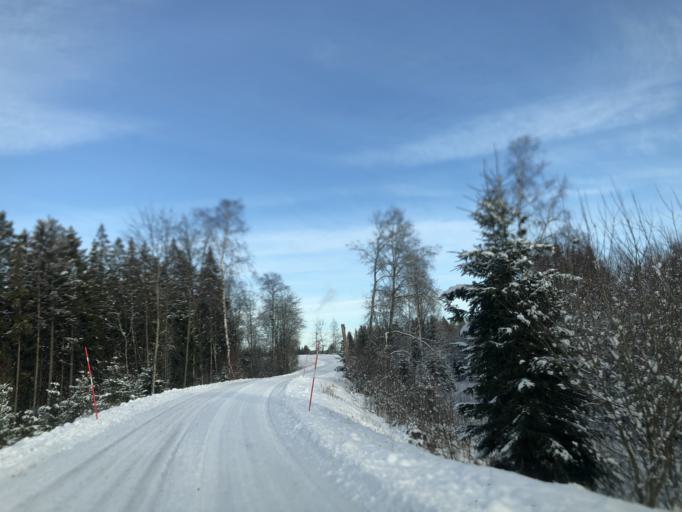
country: SE
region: Vaestra Goetaland
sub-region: Ulricehamns Kommun
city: Ulricehamn
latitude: 57.7645
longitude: 13.5175
